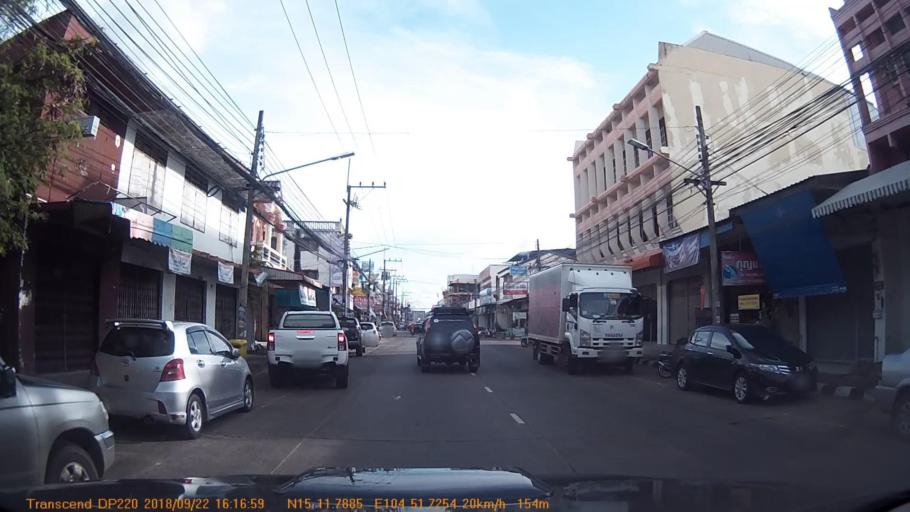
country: TH
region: Changwat Ubon Ratchathani
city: Warin Chamrap
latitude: 15.1964
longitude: 104.8621
